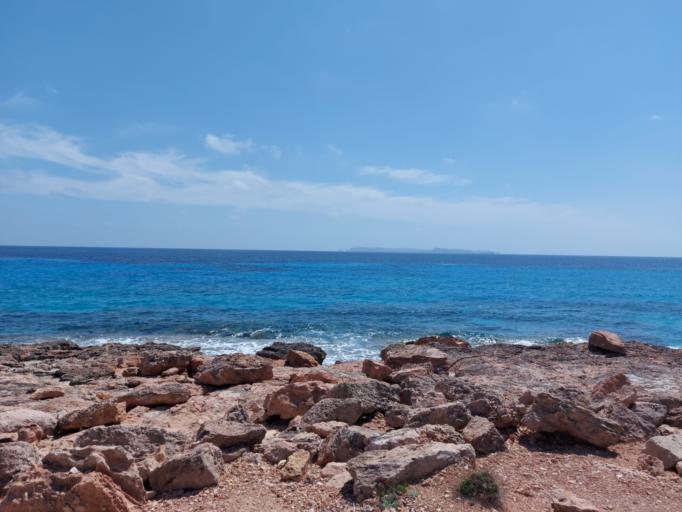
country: ES
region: Balearic Islands
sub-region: Illes Balears
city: Ses Salines
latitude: 39.2652
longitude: 3.0524
